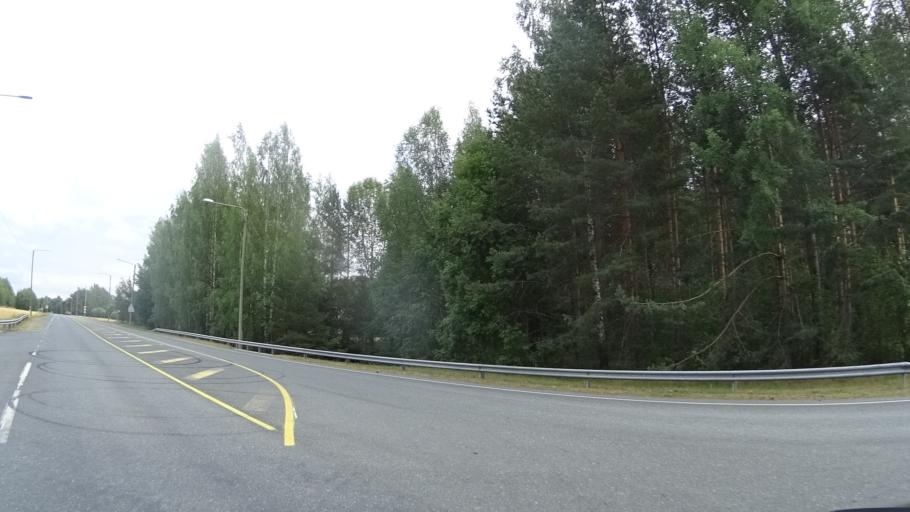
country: FI
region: Haeme
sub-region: Haemeenlinna
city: Parola
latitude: 61.0136
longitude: 24.3872
